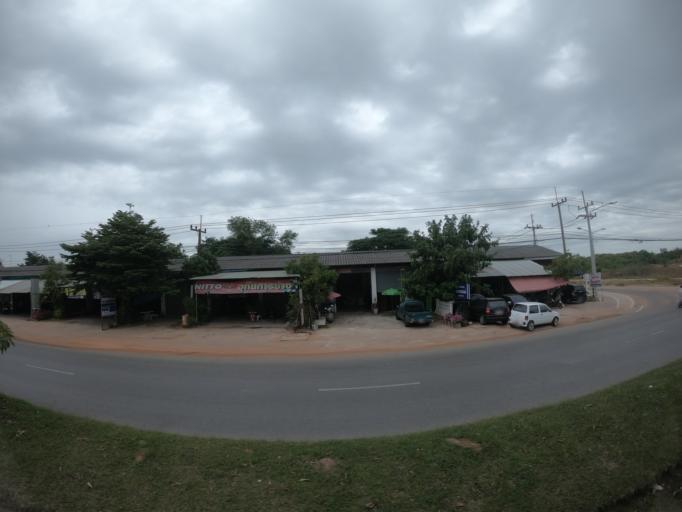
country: TH
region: Maha Sarakham
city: Maha Sarakham
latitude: 16.1695
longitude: 103.2908
